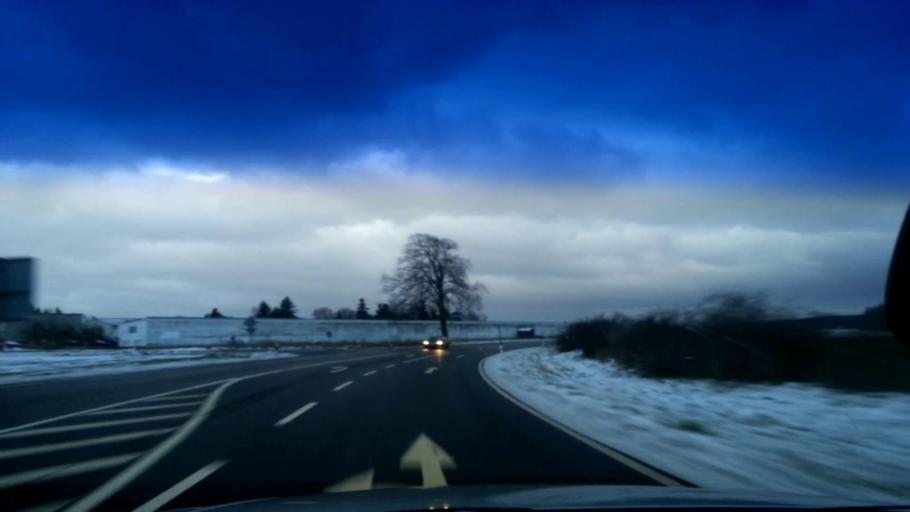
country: DE
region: Bavaria
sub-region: Upper Franconia
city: Marktleuthen
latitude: 50.1380
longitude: 12.0125
